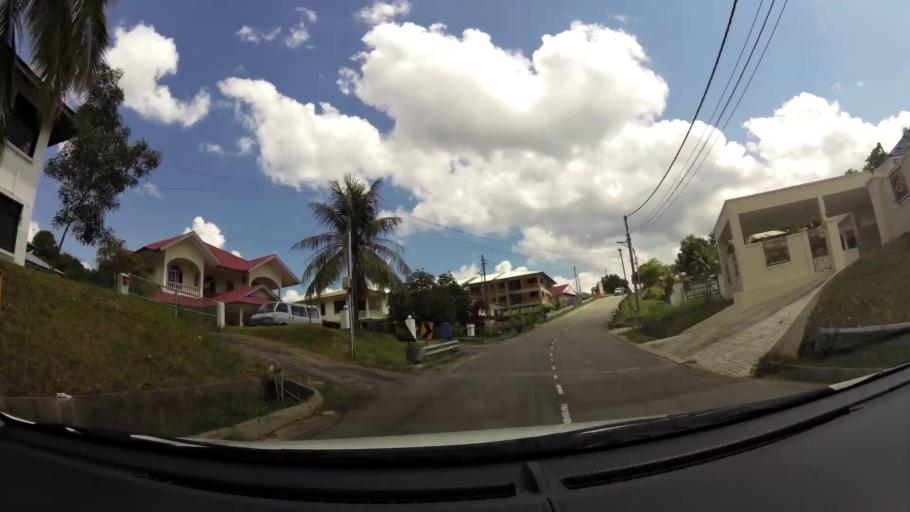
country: BN
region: Brunei and Muara
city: Bandar Seri Begawan
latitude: 4.9417
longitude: 114.9669
